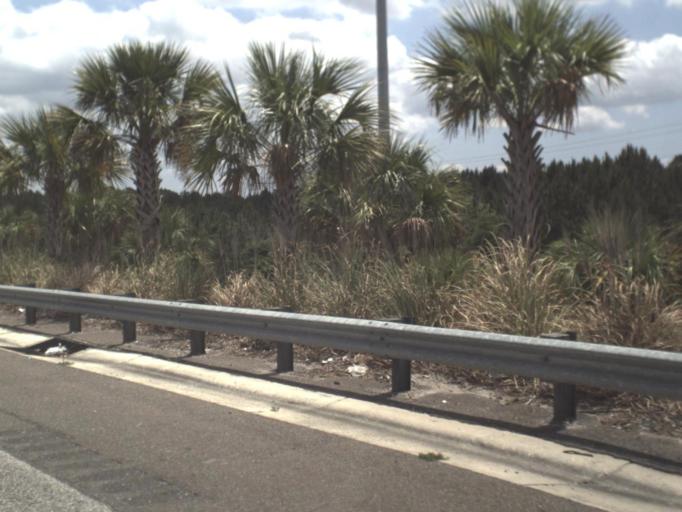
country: US
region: Florida
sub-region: Duval County
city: Jacksonville Beach
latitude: 30.2679
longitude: -81.5205
